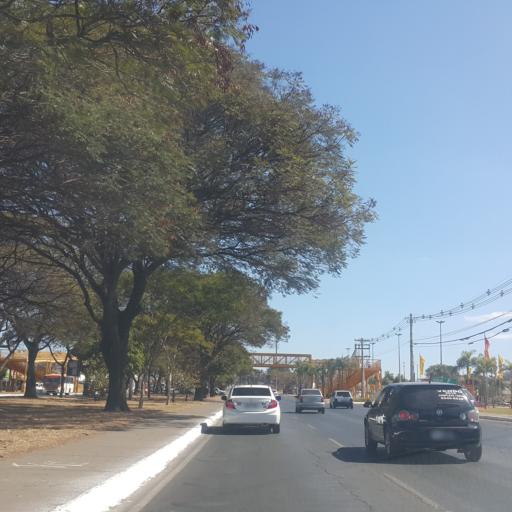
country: BR
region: Federal District
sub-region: Brasilia
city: Brasilia
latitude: -15.8108
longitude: -48.0917
